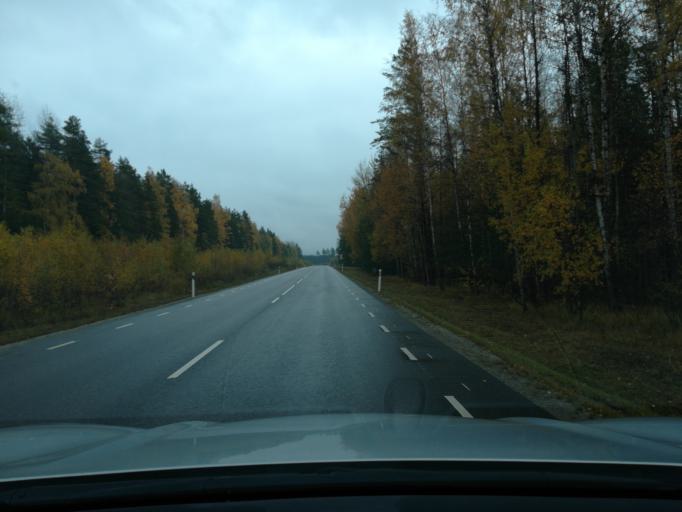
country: EE
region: Ida-Virumaa
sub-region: Johvi vald
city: Johvi
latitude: 59.3053
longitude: 27.4630
